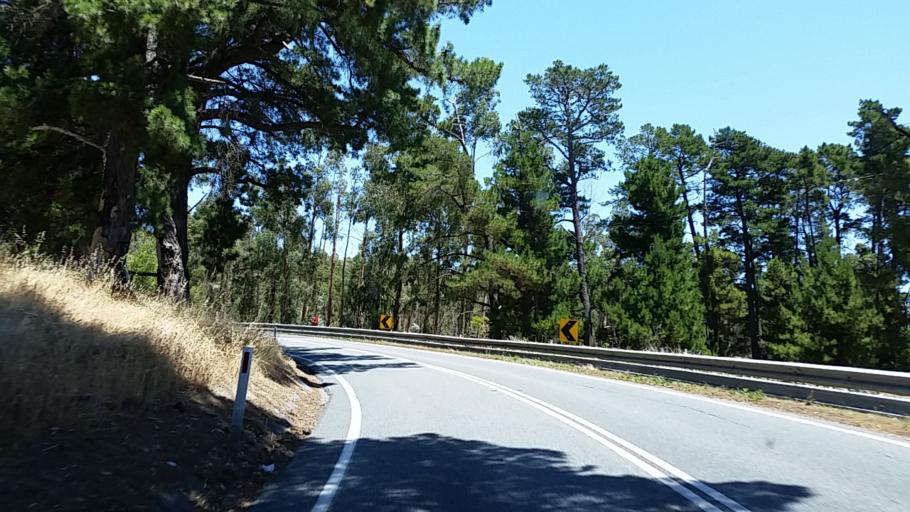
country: AU
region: South Australia
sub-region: Tea Tree Gully
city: Golden Grove
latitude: -34.8236
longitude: 138.7680
